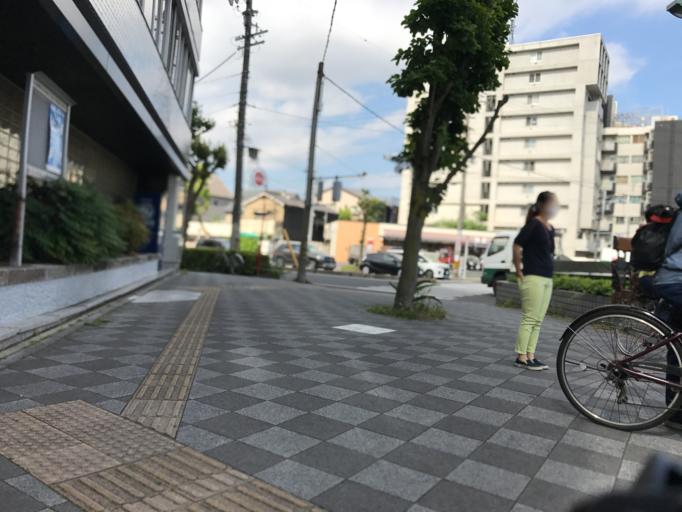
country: JP
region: Aichi
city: Nagoya-shi
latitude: 35.1821
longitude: 136.9343
